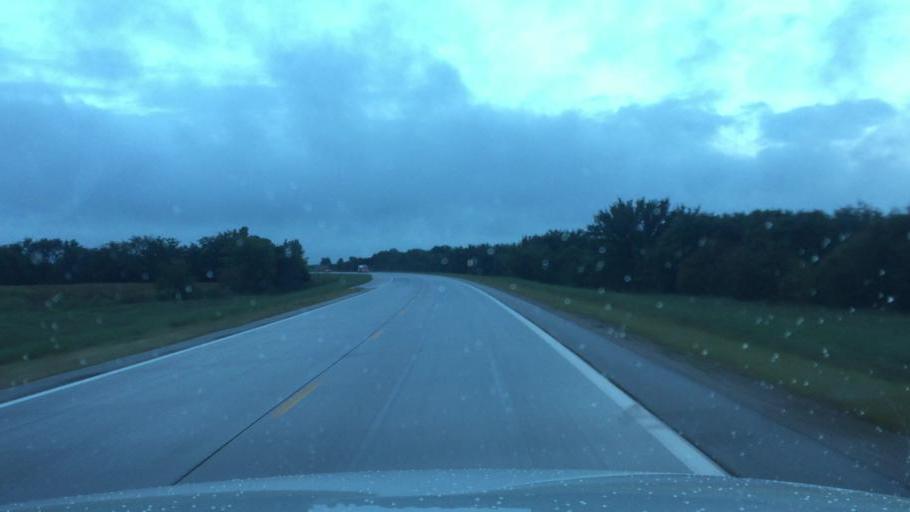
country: US
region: Kansas
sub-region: Neosho County
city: Chanute
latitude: 37.7201
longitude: -95.4771
